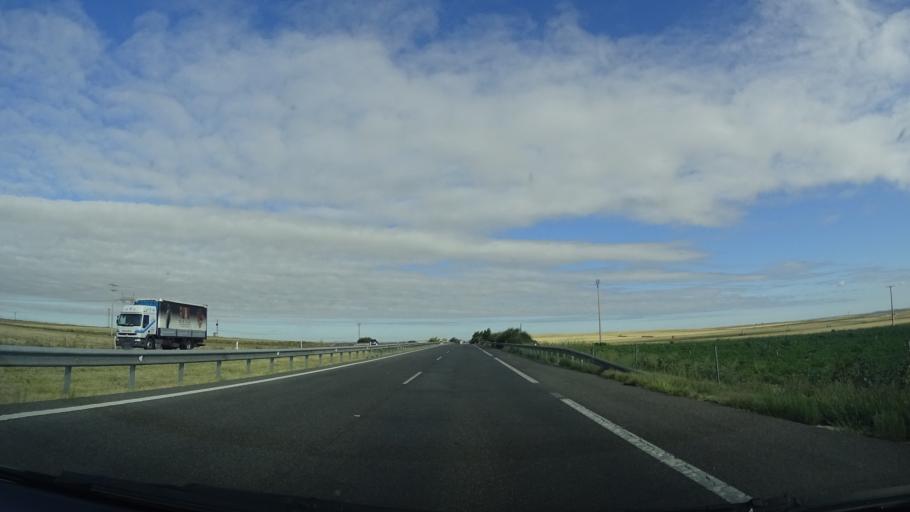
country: ES
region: Castille and Leon
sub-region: Provincia de Valladolid
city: Ataquines
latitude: 41.1967
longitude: -4.8186
